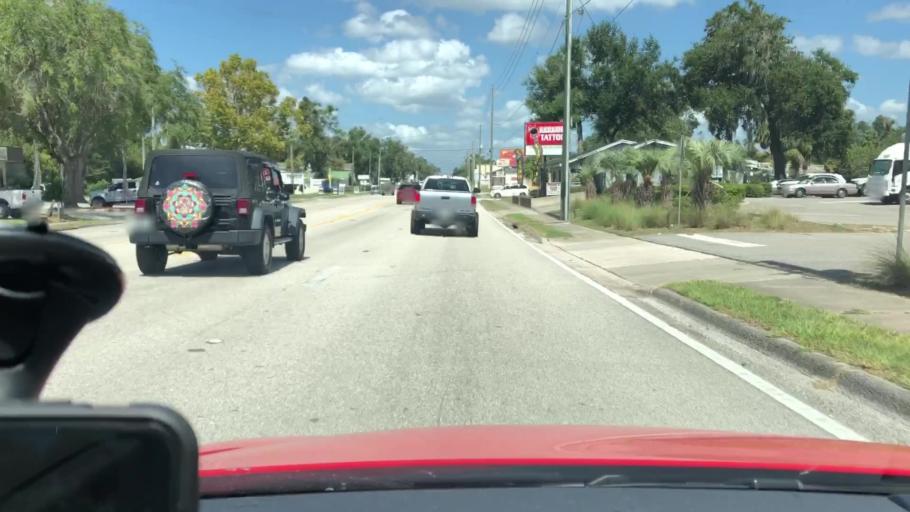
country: US
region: Florida
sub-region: Volusia County
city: West DeLand
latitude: 29.0234
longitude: -81.3240
